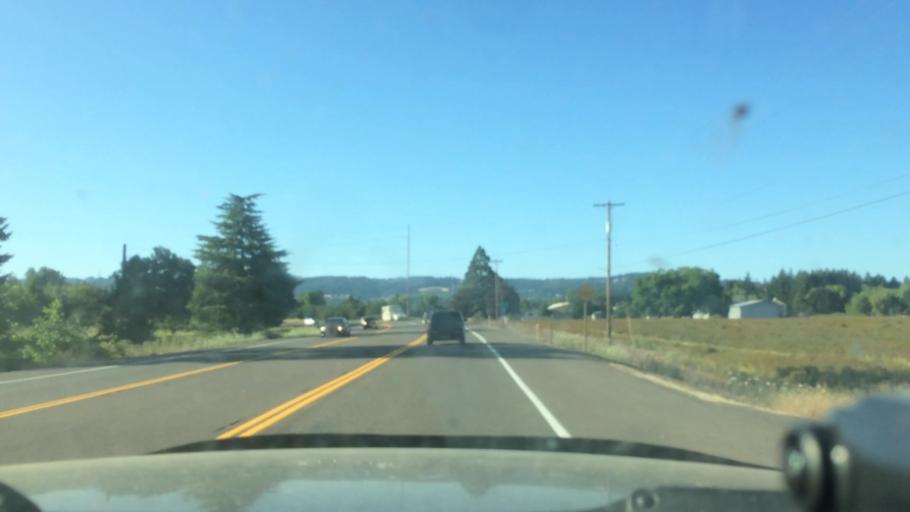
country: US
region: Oregon
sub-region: Yamhill County
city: Newberg
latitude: 45.2844
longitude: -122.9453
